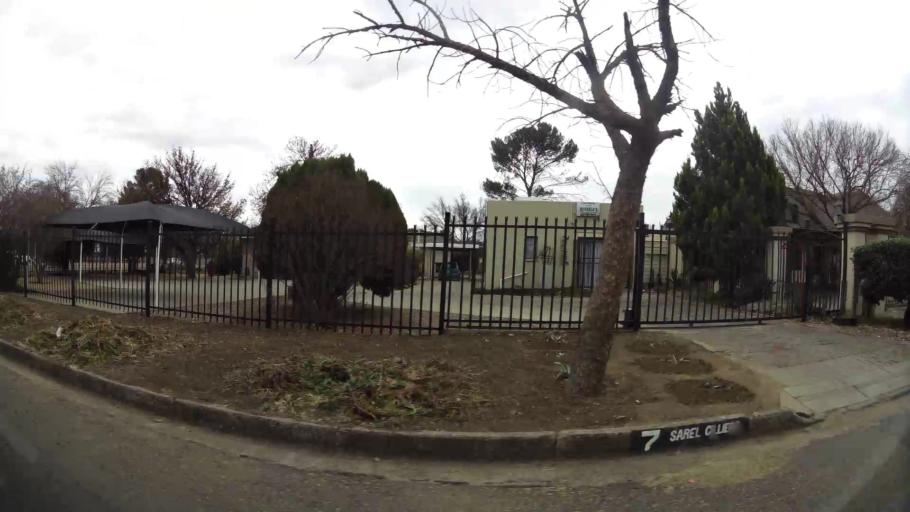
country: ZA
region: Orange Free State
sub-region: Fezile Dabi District Municipality
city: Kroonstad
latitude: -27.6762
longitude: 27.2401
